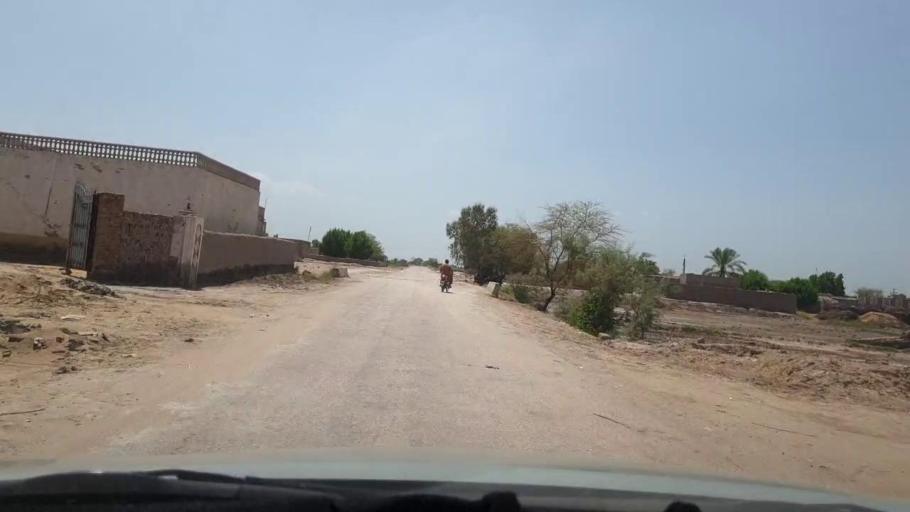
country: PK
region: Sindh
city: Pano Aqil
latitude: 27.6635
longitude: 69.1344
